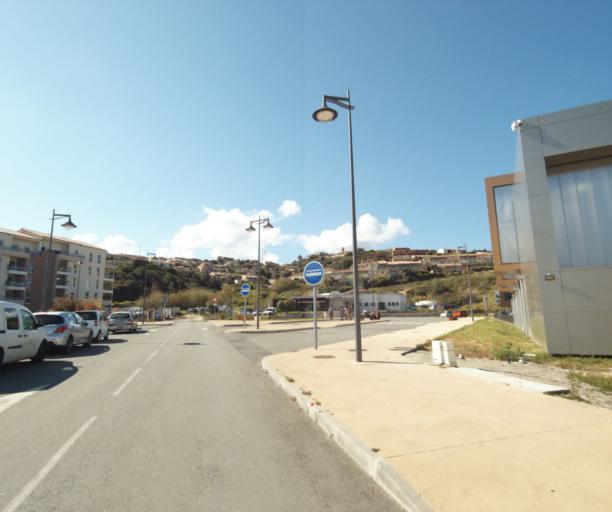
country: FR
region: Corsica
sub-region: Departement de la Corse-du-Sud
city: Propriano
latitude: 41.6735
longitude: 8.9009
